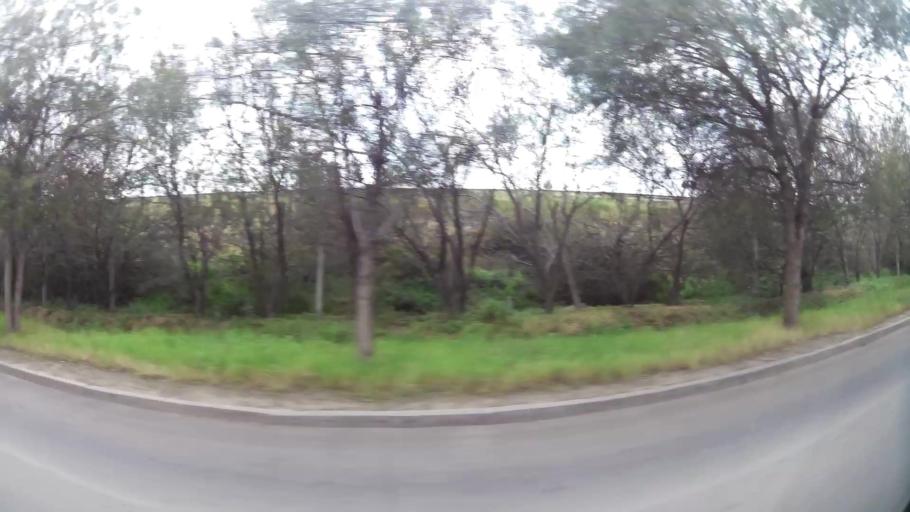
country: CL
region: Santiago Metropolitan
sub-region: Provincia de Chacabuco
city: Chicureo Abajo
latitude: -33.2058
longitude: -70.6657
